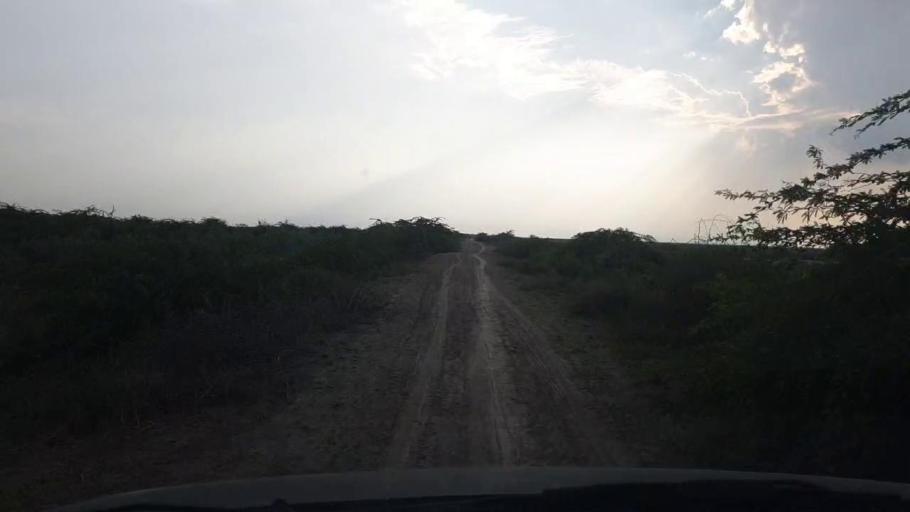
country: PK
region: Sindh
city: Badin
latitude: 24.4662
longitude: 68.6936
